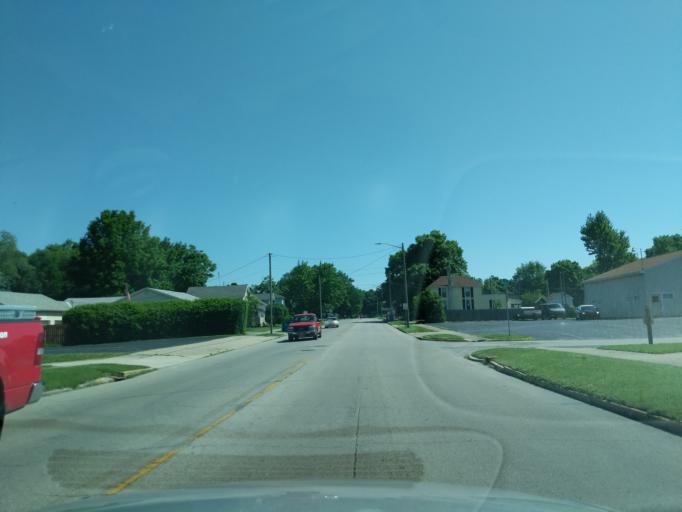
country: US
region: Indiana
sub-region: Huntington County
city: Huntington
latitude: 40.8705
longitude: -85.4999
